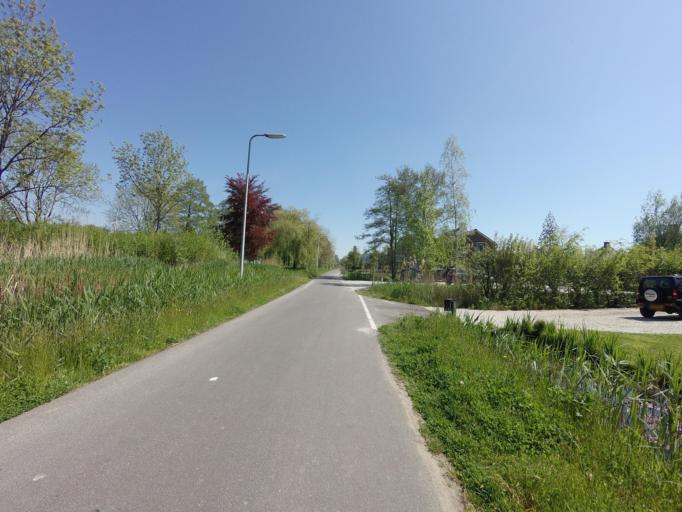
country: NL
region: South Holland
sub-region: Gemeente Gouda
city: Gouda
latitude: 52.0171
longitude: 4.7357
